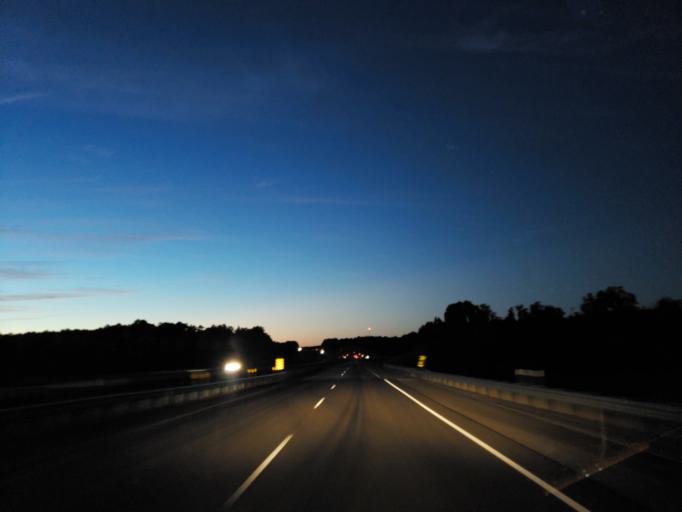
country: US
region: Mississippi
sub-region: Clarke County
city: Quitman
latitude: 32.0967
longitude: -88.7034
